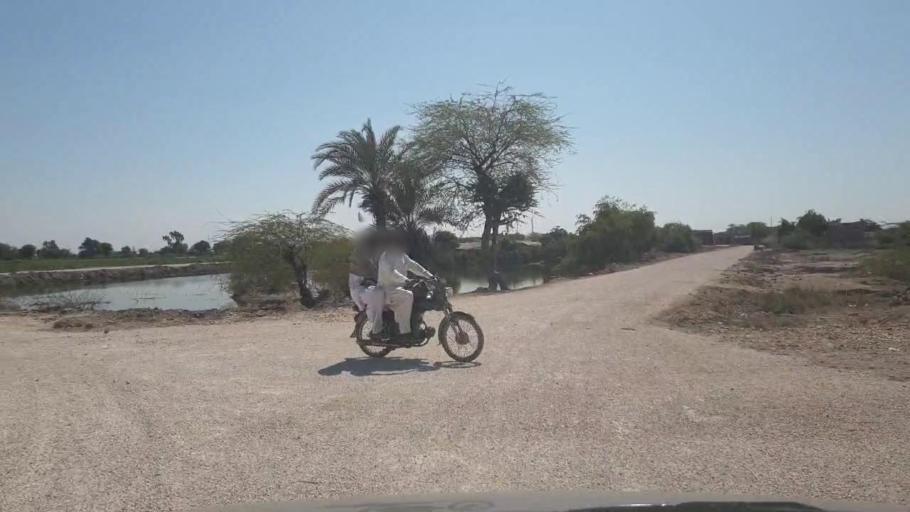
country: PK
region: Sindh
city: Dhoro Naro
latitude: 25.4520
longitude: 69.6011
